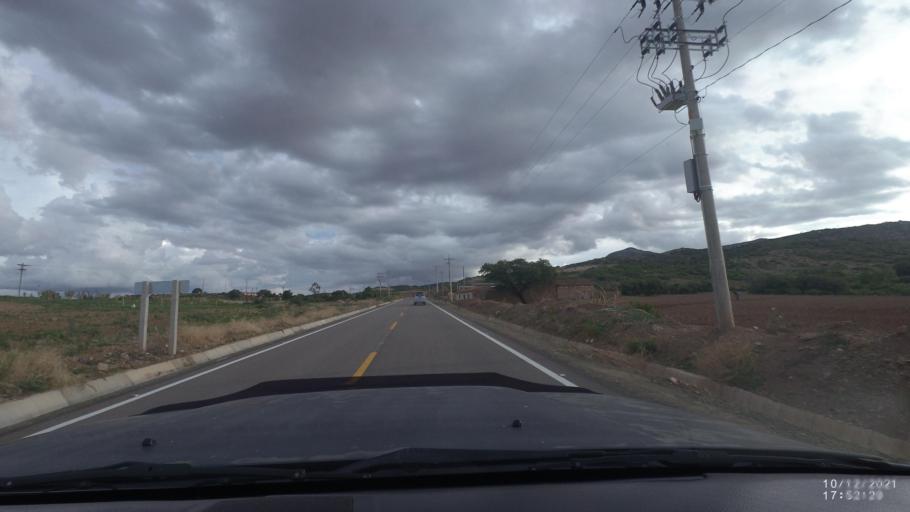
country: BO
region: Cochabamba
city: Cliza
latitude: -17.6855
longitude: -65.9518
